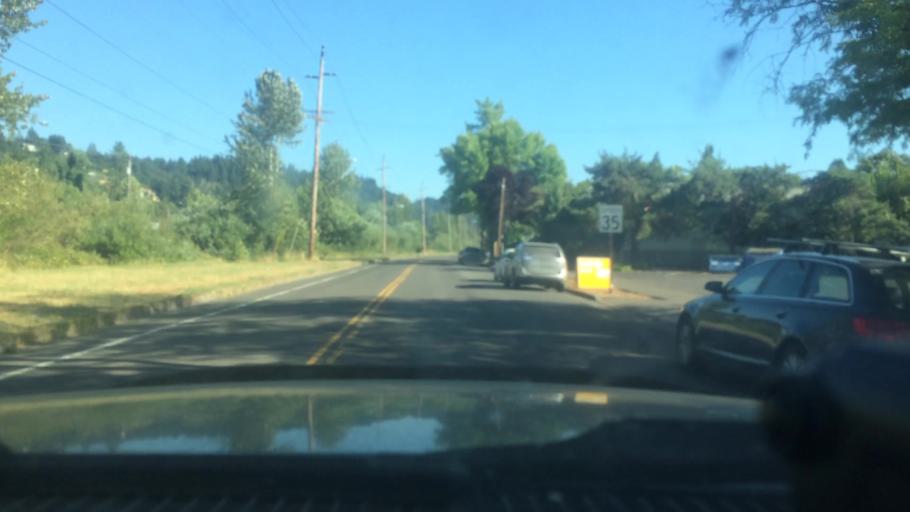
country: US
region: Oregon
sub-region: Lane County
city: Eugene
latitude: 44.0192
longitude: -123.0806
